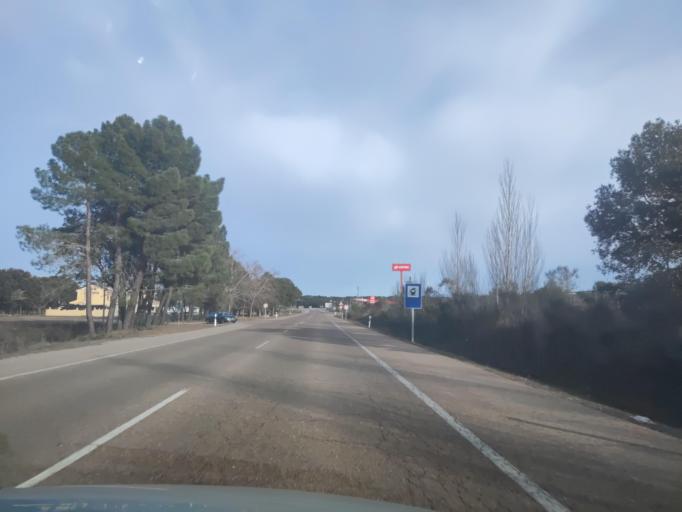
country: ES
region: Castille and Leon
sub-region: Provincia de Salamanca
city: Espeja
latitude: 40.5910
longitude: -6.7103
